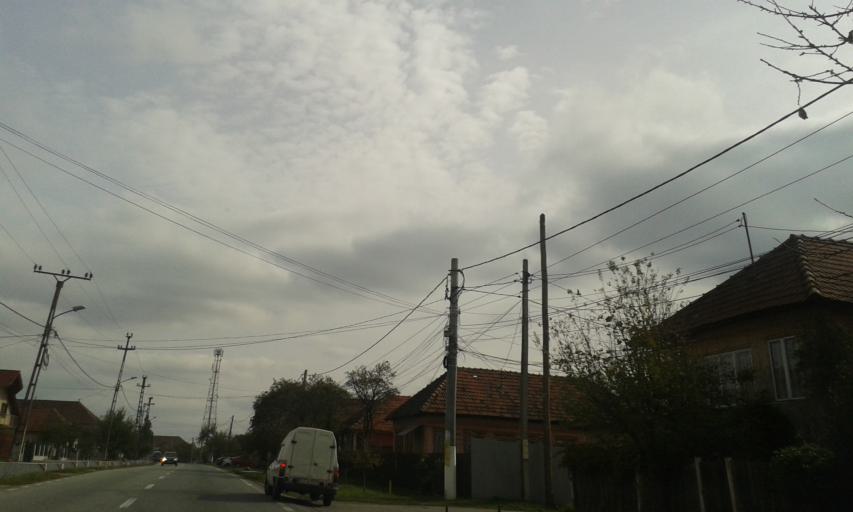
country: RO
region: Gorj
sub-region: Comuna Balanesti
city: Balanesti
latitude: 45.0422
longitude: 23.3490
